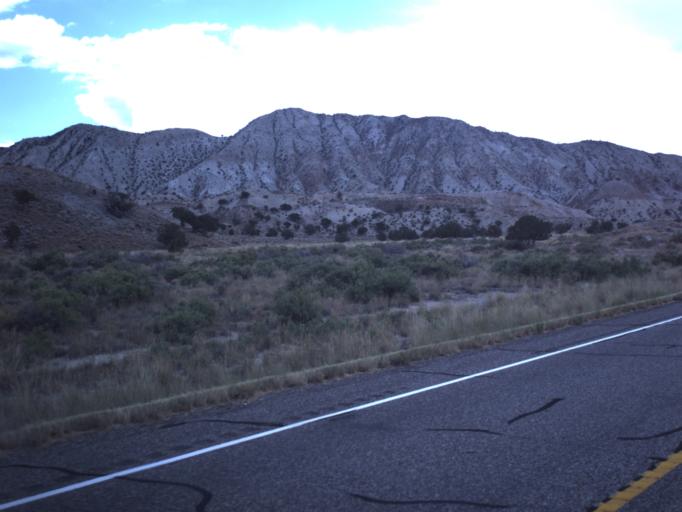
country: US
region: Utah
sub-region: Sevier County
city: Aurora
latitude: 38.8178
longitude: -111.9406
